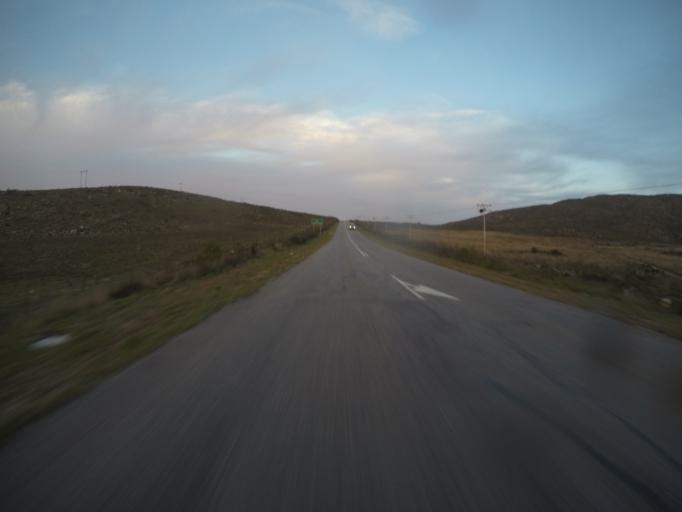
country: ZA
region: Western Cape
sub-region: Eden District Municipality
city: Plettenberg Bay
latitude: -33.7429
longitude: 23.4473
